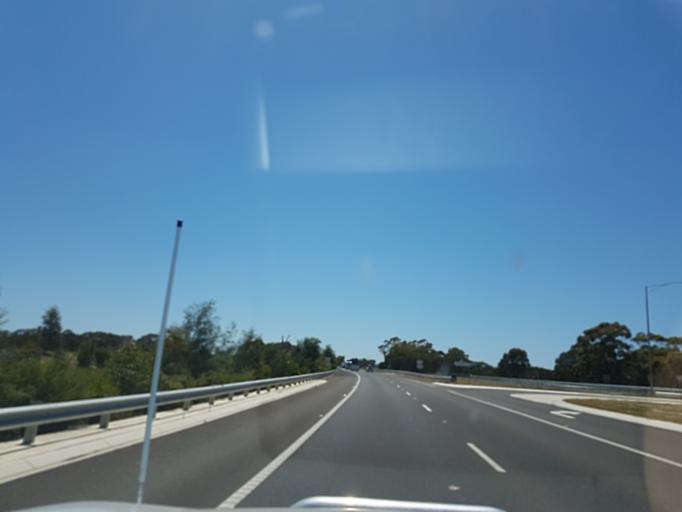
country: AU
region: Victoria
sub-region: Wellington
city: Heyfield
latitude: -38.1545
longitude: 146.7635
